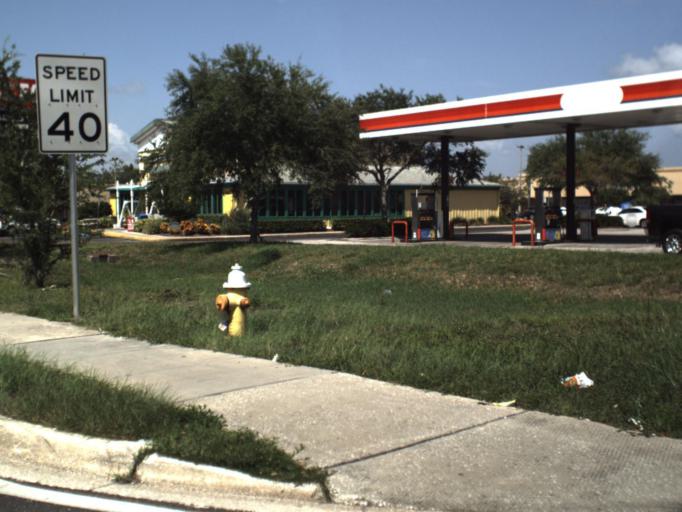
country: US
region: Florida
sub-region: Pinellas County
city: Clearwater
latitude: 27.9514
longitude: -82.7875
